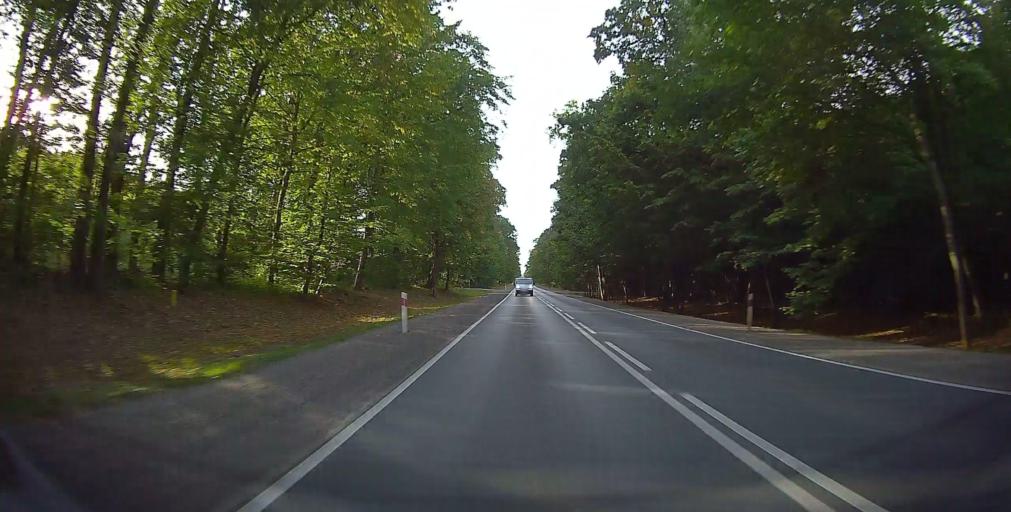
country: PL
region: Masovian Voivodeship
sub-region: Powiat piaseczynski
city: Zabieniec
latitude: 52.0461
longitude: 21.0751
